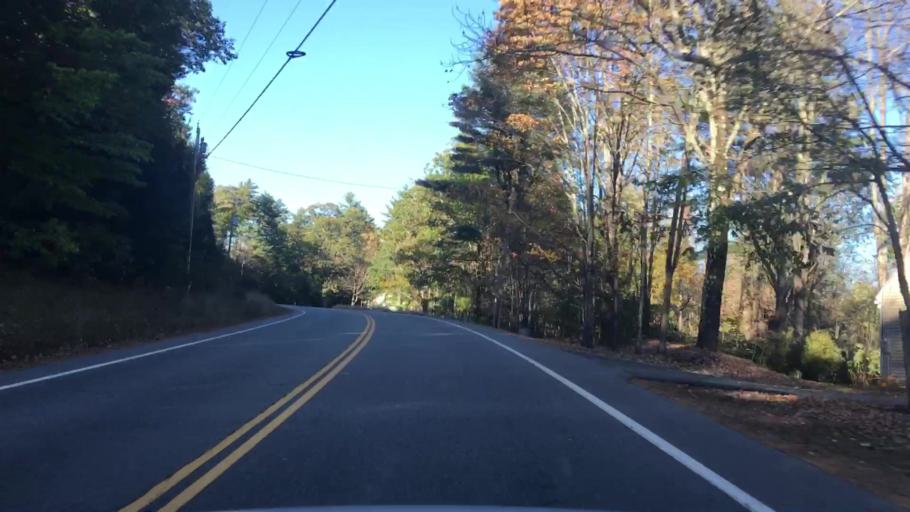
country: US
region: New Hampshire
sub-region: Merrimack County
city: Contoocook
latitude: 43.2636
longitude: -71.7295
